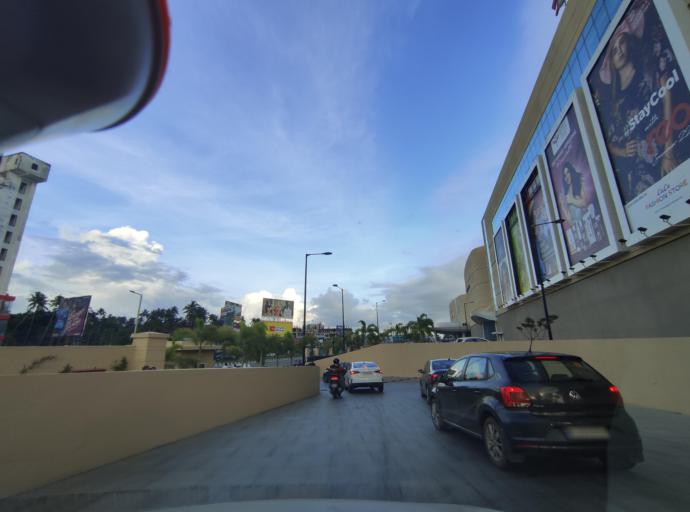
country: IN
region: Kerala
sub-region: Thiruvananthapuram
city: Thiruvananthapuram
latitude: 8.5156
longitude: 76.8976
